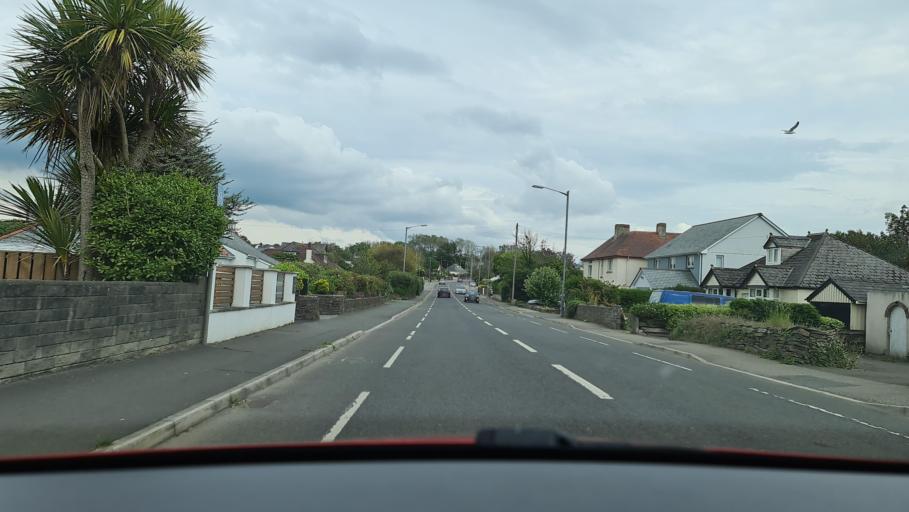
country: GB
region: England
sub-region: Cornwall
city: Bude
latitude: 50.8213
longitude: -4.5384
